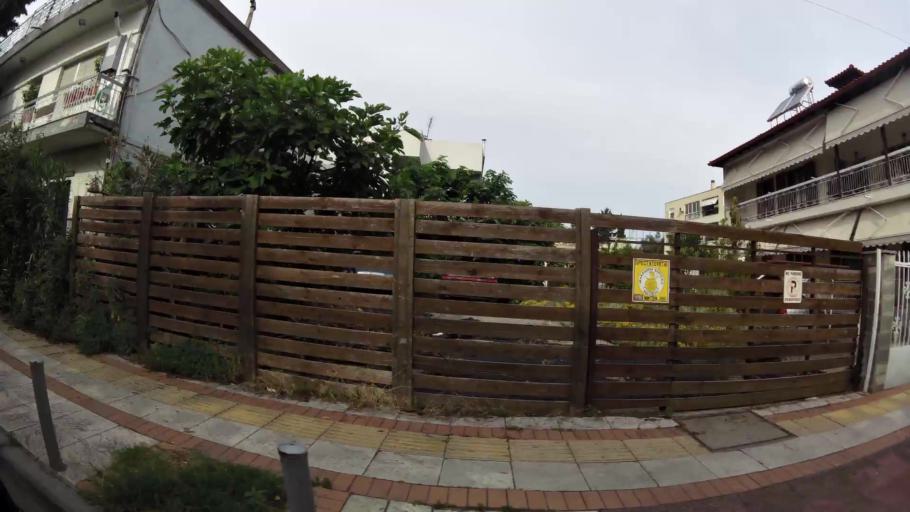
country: GR
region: Central Macedonia
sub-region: Nomos Thessalonikis
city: Thermi
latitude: 40.5503
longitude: 23.0189
